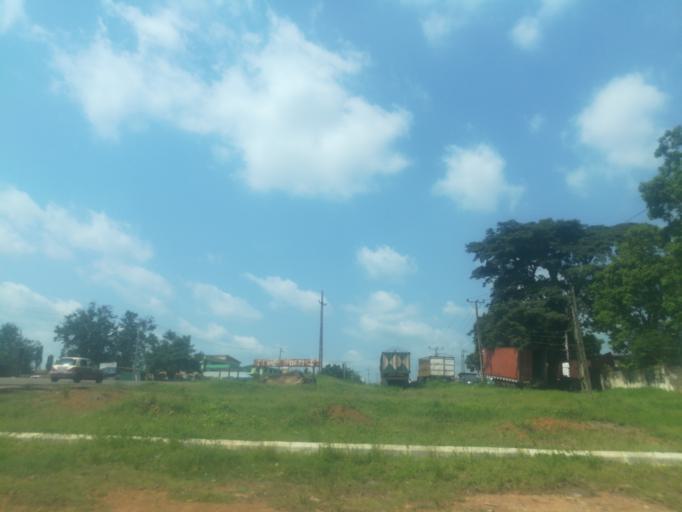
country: NG
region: Oyo
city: Moniya
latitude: 7.5096
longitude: 3.9128
